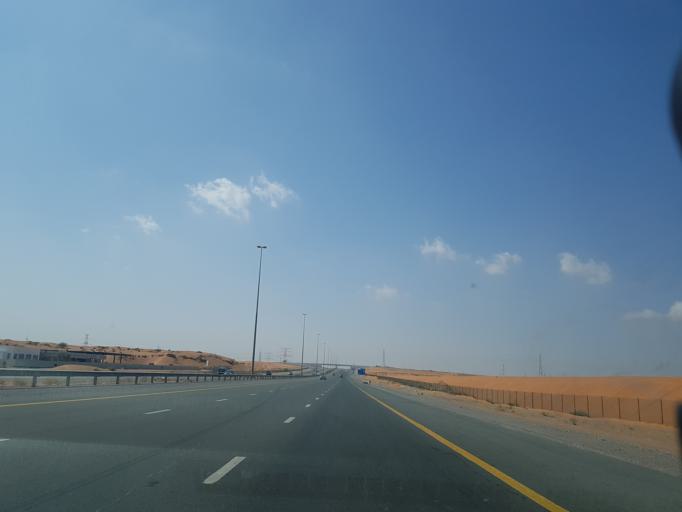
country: AE
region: Ra's al Khaymah
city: Ras al-Khaimah
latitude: 25.7026
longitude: 55.9346
